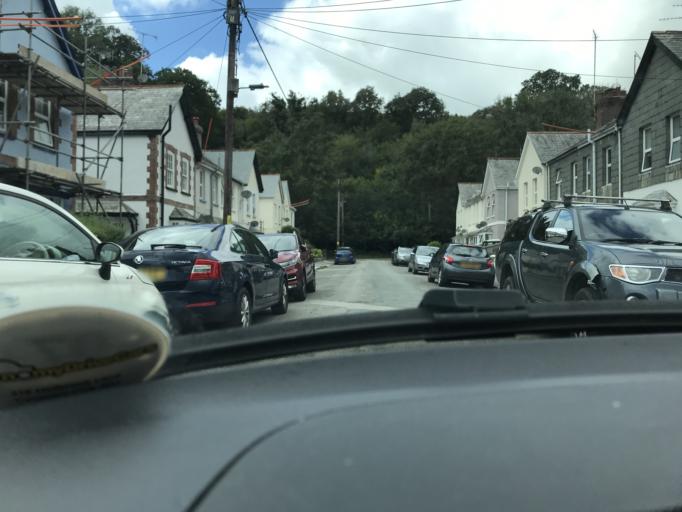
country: GB
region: England
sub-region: Devon
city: Tavistock
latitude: 50.5536
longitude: -4.1356
